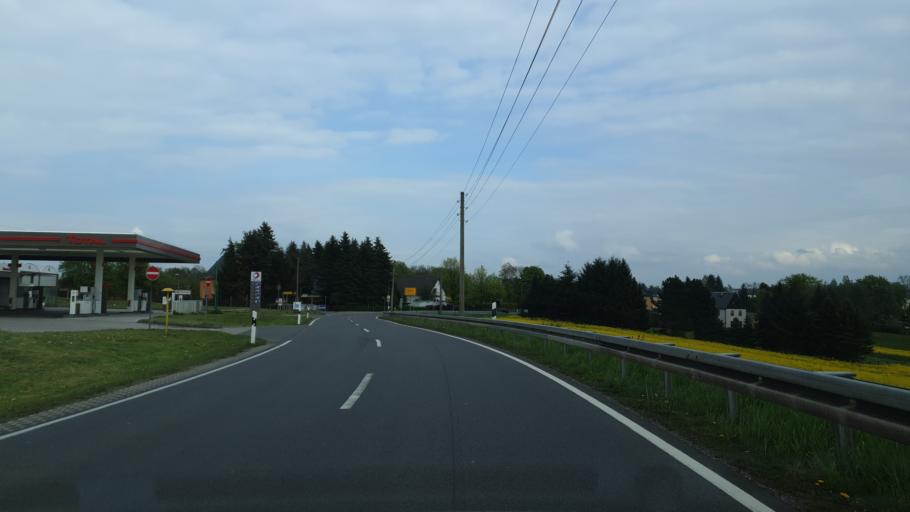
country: DE
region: Saxony
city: Lugau
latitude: 50.7465
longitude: 12.7411
